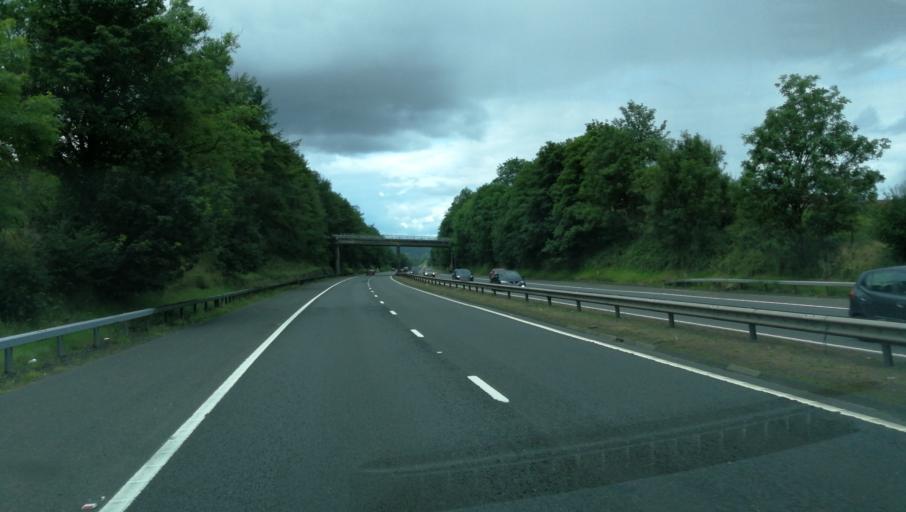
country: GB
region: Scotland
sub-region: Falkirk
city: Dunipace
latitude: 56.0132
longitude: -3.9212
